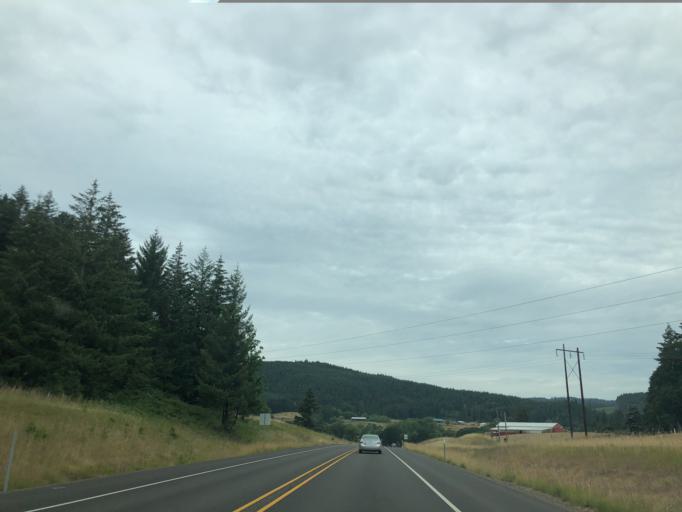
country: US
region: Oregon
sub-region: Benton County
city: Philomath
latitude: 44.5894
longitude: -123.4335
